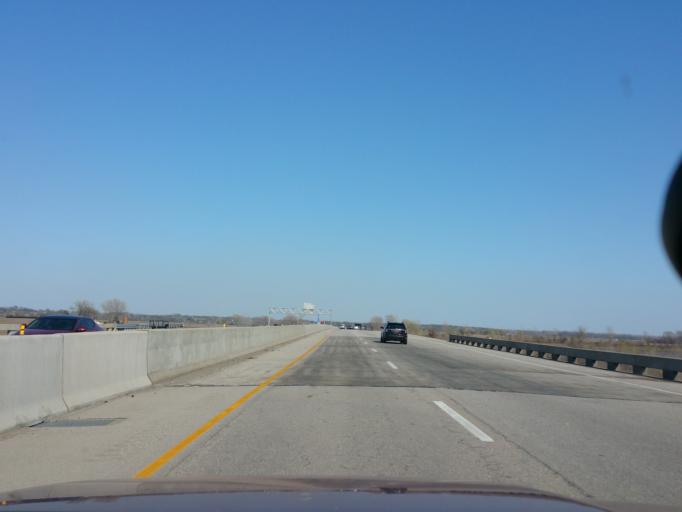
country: US
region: Kansas
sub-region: Douglas County
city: Lawrence
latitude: 38.9937
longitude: -95.2140
